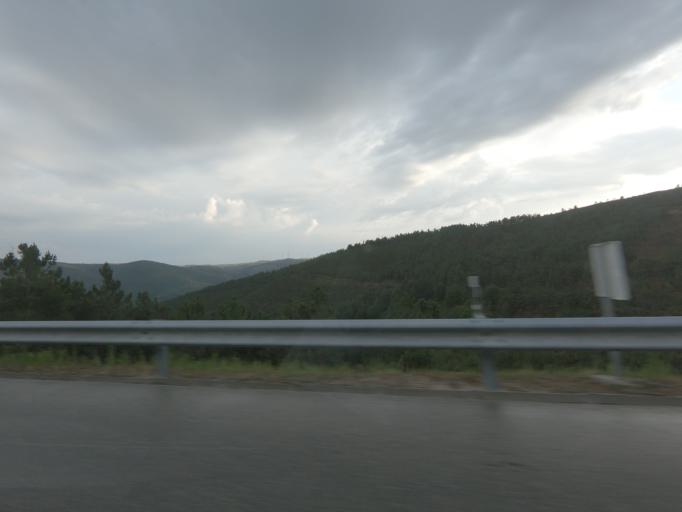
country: PT
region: Viseu
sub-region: Lamego
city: Lamego
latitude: 41.0485
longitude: -7.8481
